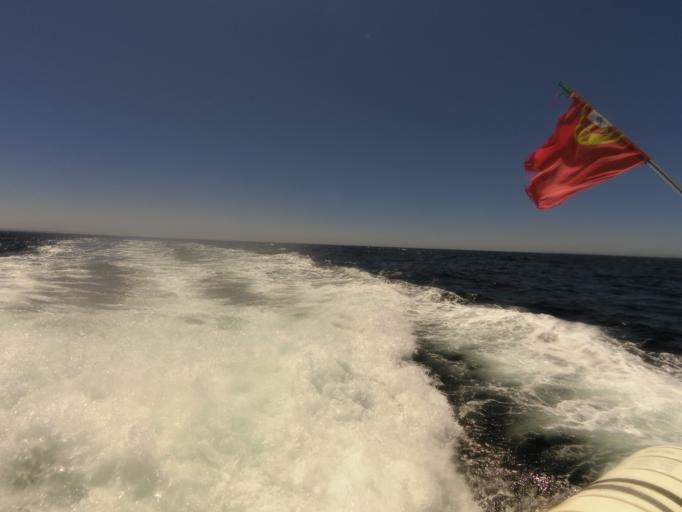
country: PT
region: Leiria
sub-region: Peniche
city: Peniche
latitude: 39.4070
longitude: -9.4971
